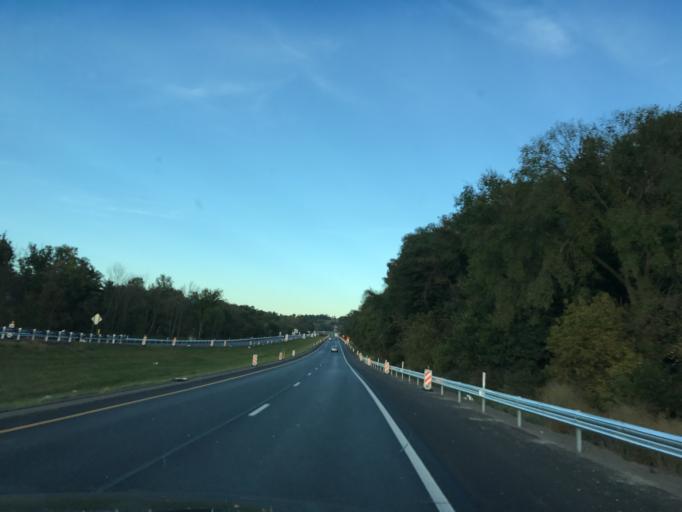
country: US
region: Pennsylvania
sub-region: Washington County
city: Wolfdale
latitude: 40.1148
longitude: -80.4136
